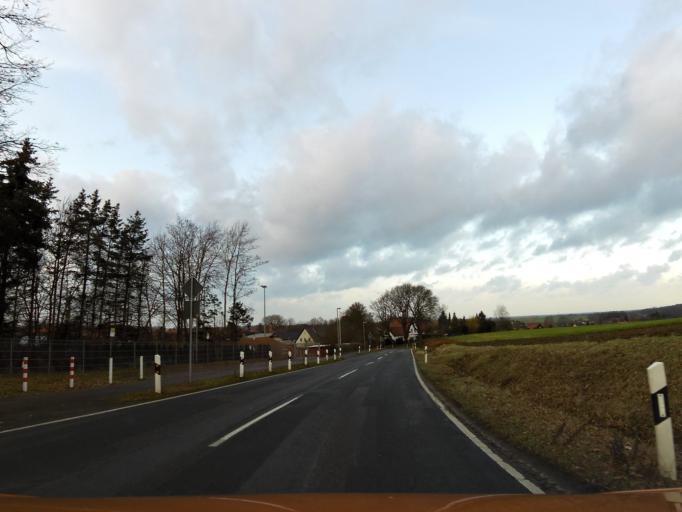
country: DE
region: Lower Saxony
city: Gross Twulpstedt
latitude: 52.3875
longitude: 10.8572
